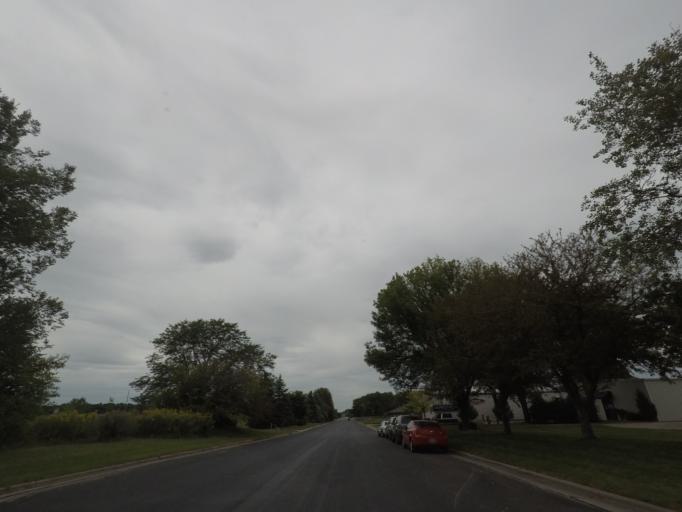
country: US
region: Wisconsin
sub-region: Dane County
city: Middleton
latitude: 43.1080
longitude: -89.5144
